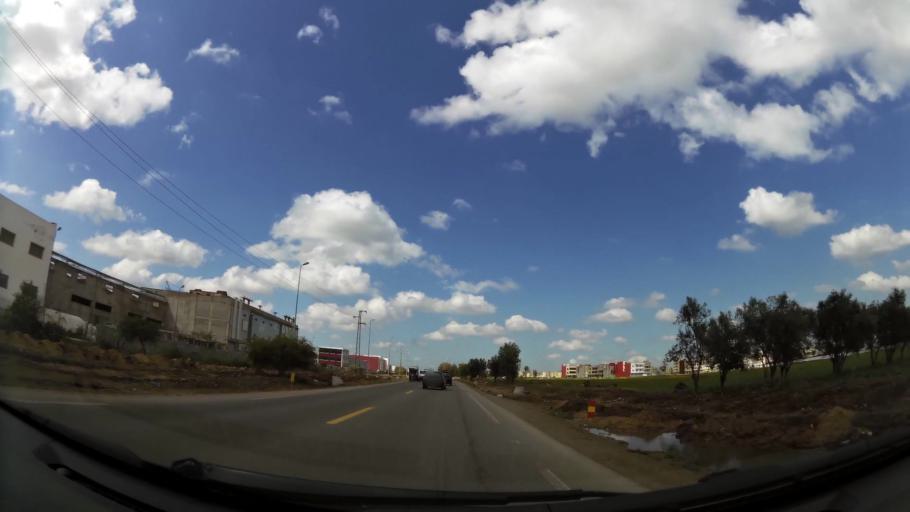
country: MA
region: Grand Casablanca
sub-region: Mediouna
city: Mediouna
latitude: 33.3914
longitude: -7.5355
